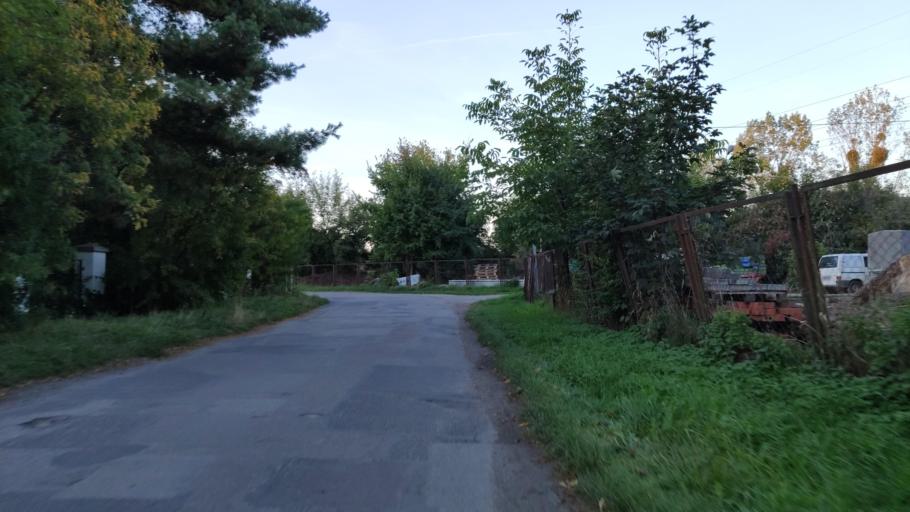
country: PL
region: Lower Silesian Voivodeship
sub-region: Powiat wroclawski
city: Wroclaw
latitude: 51.0795
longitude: 17.0317
